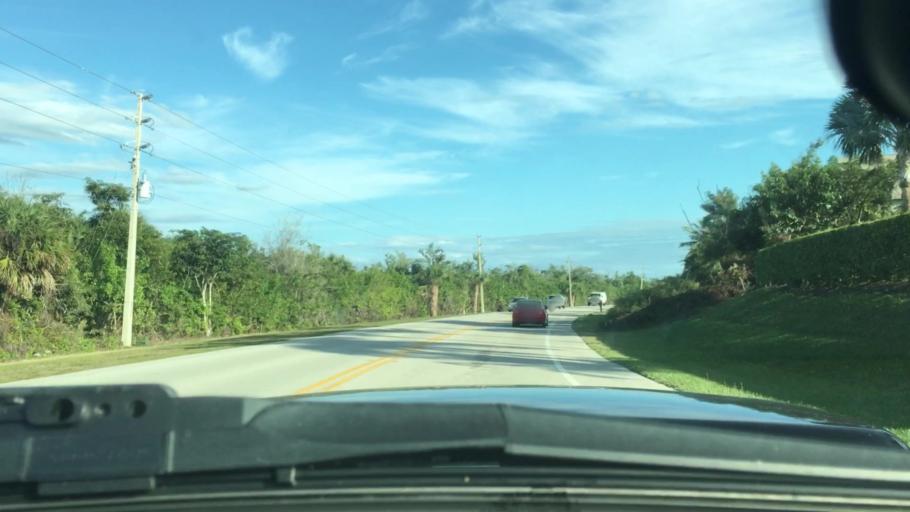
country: US
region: Florida
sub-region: Collier County
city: Marco
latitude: 25.9380
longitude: -81.6841
